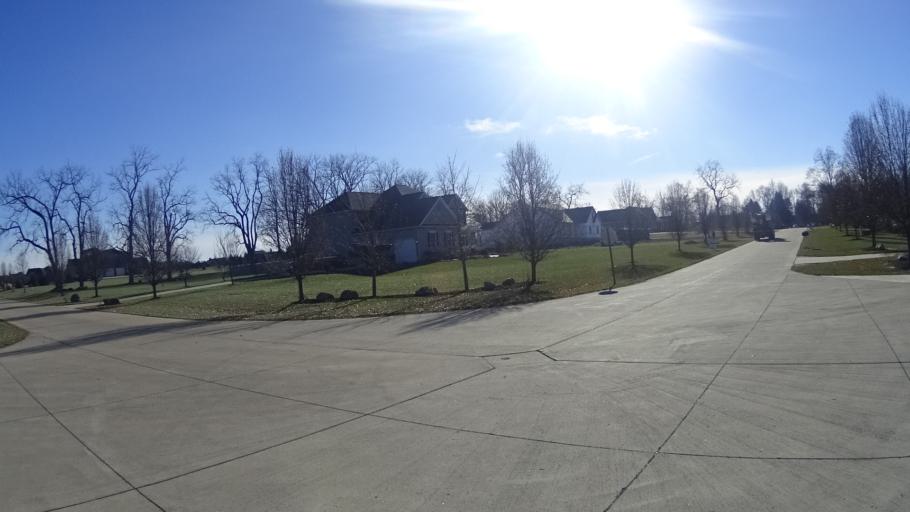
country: US
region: Ohio
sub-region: Lorain County
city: South Amherst
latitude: 41.3782
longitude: -82.2901
